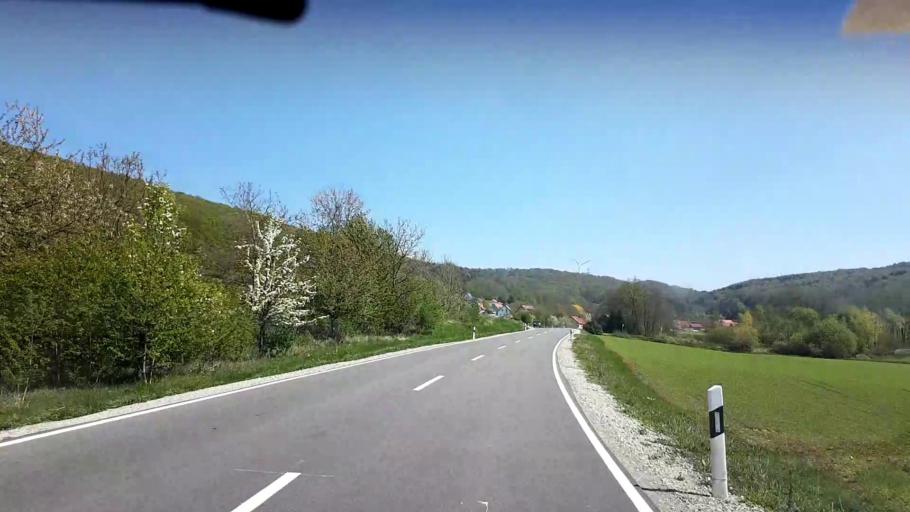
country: DE
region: Bavaria
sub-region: Upper Franconia
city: Schesslitz
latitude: 49.9801
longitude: 11.0745
